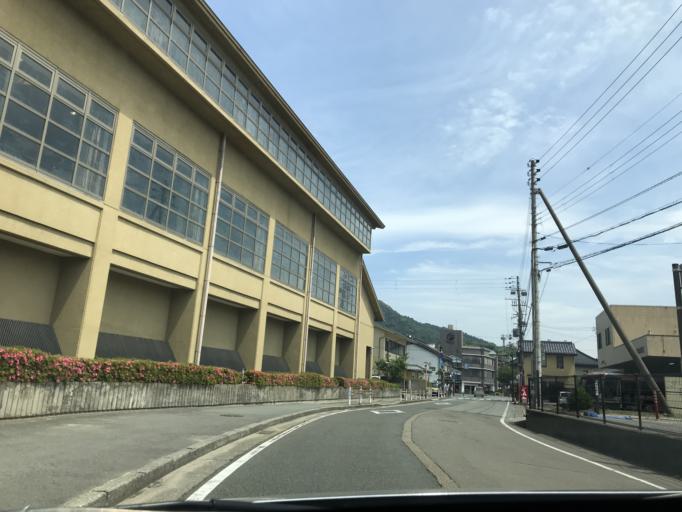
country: JP
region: Hyogo
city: Toyooka
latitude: 35.6228
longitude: 134.8128
